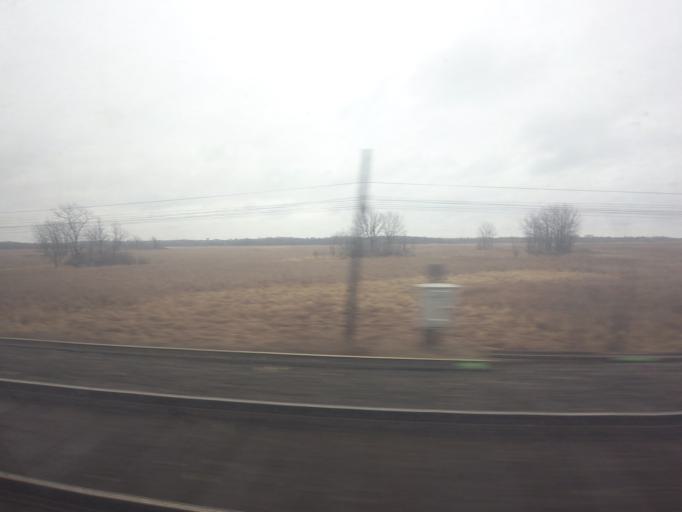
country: CA
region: Ontario
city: Kingston
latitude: 44.2765
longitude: -76.4714
